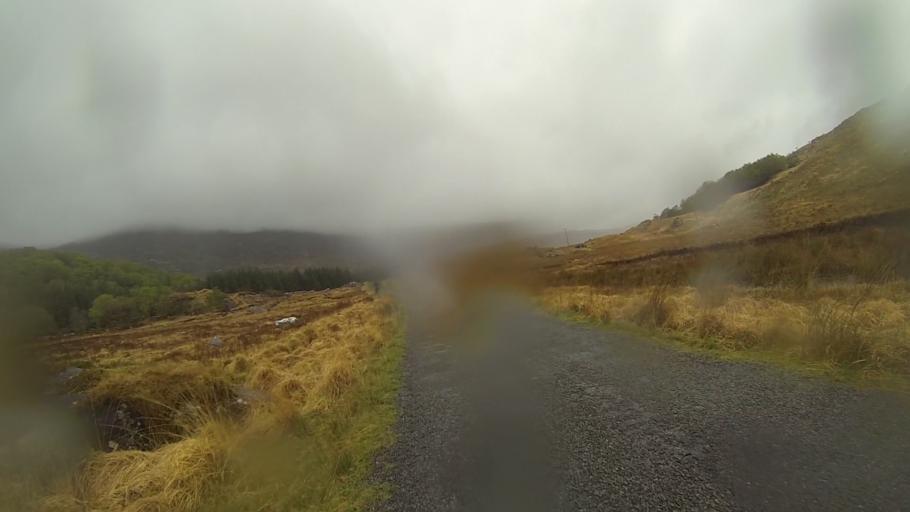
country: IE
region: Munster
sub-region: Ciarrai
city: Kenmare
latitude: 51.9559
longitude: -9.6366
